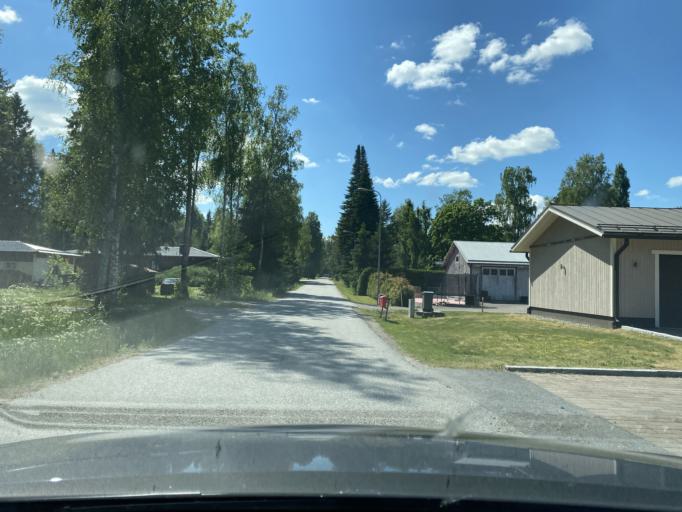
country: FI
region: Satakunta
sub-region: Rauma
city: Eura
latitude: 61.1121
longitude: 22.1349
